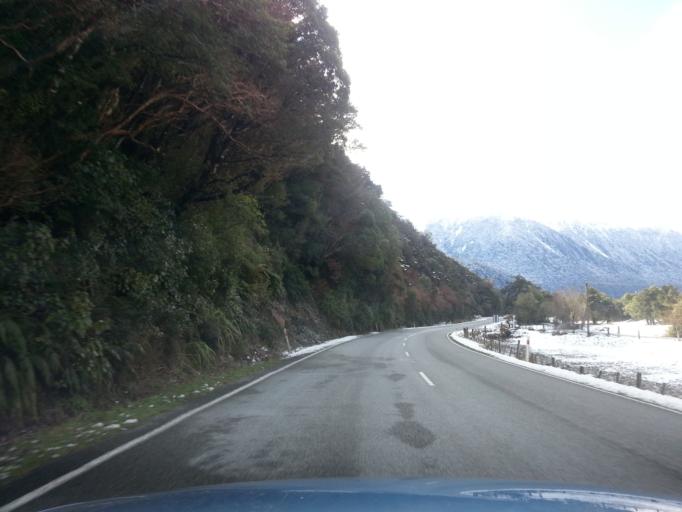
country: NZ
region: West Coast
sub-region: Grey District
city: Greymouth
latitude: -42.8298
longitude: 171.5611
